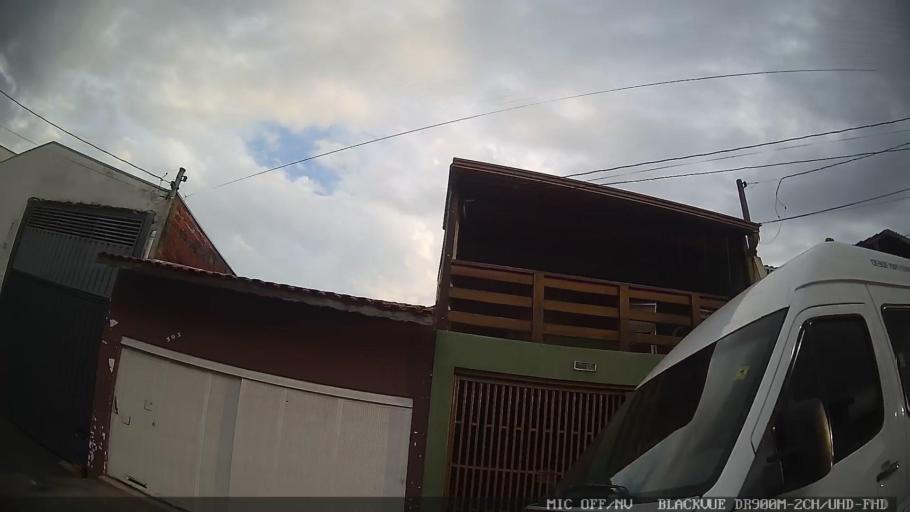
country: BR
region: Sao Paulo
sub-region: Indaiatuba
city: Indaiatuba
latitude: -23.1281
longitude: -47.2359
